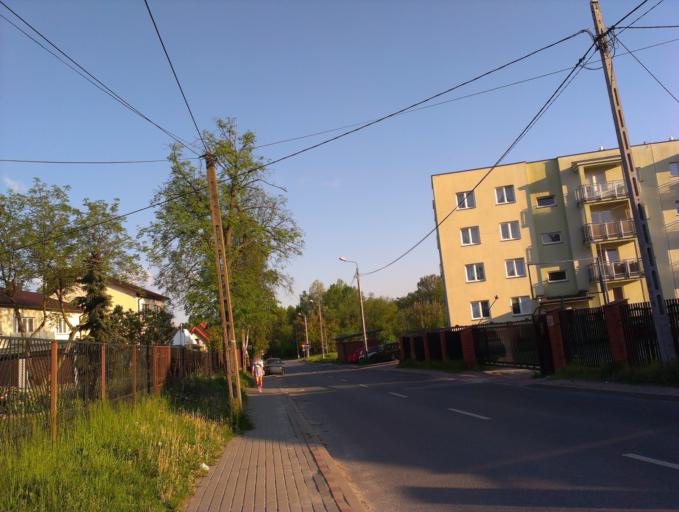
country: PL
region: Masovian Voivodeship
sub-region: Powiat piaseczynski
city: Zabieniec
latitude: 52.0626
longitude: 21.0307
